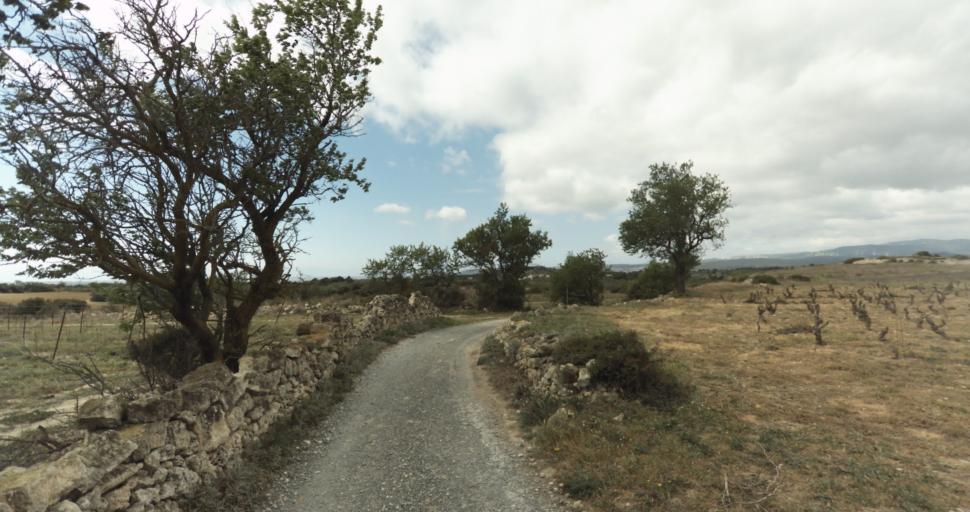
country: FR
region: Languedoc-Roussillon
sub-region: Departement de l'Aude
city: Leucate
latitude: 42.9161
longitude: 3.0389
